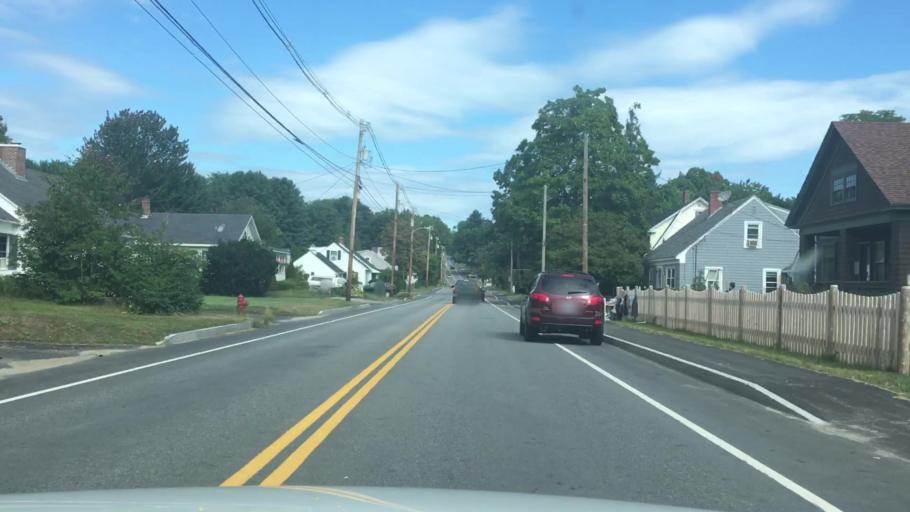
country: US
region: Maine
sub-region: Androscoggin County
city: Auburn
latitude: 44.1059
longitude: -70.2485
